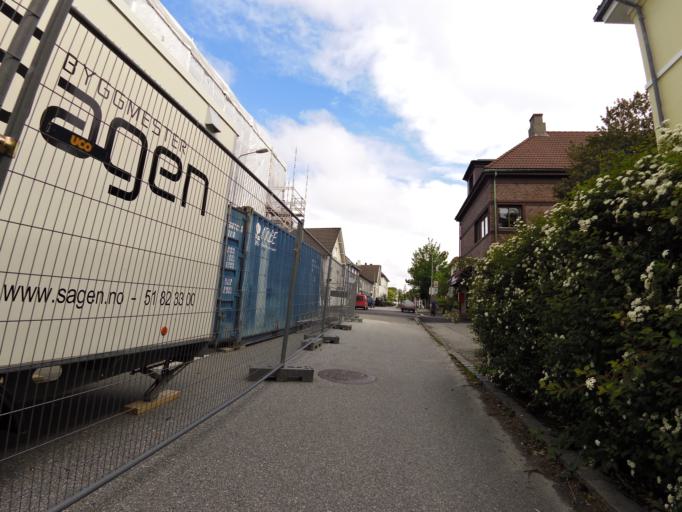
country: NO
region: Rogaland
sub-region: Stavanger
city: Stavanger
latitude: 58.9673
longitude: 5.7258
